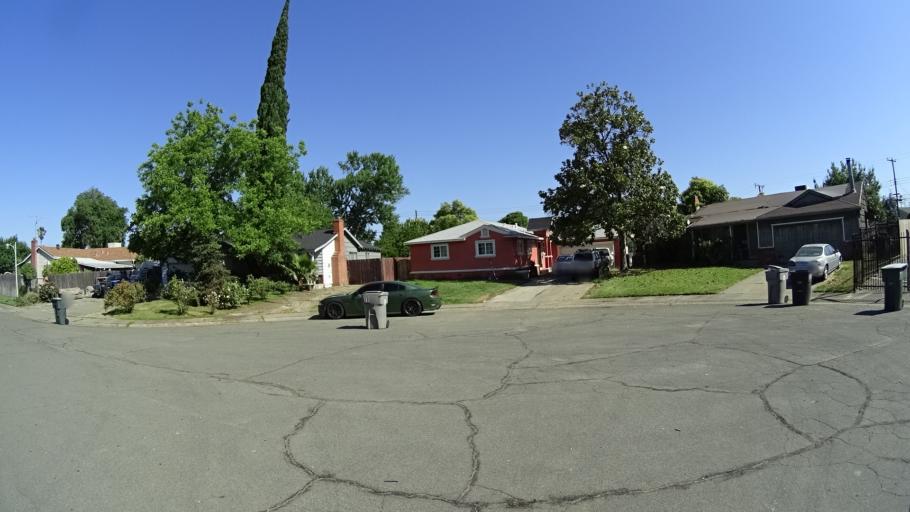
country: US
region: California
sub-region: Sacramento County
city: Florin
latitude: 38.5308
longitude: -121.4119
